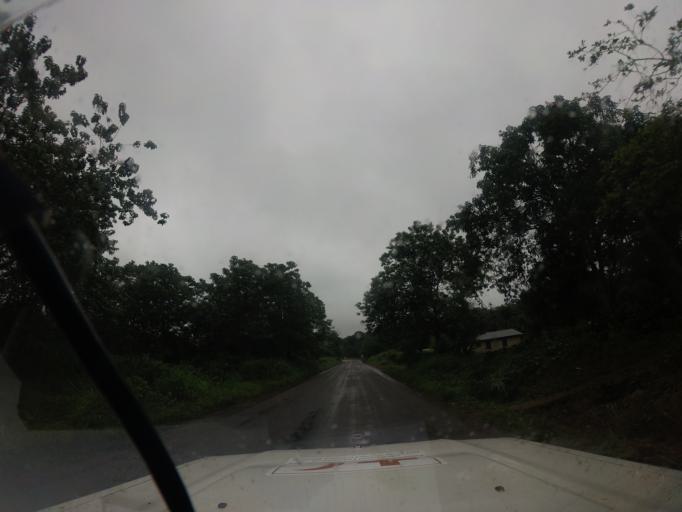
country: SL
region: Northern Province
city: Kabala
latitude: 9.5383
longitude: -11.5794
